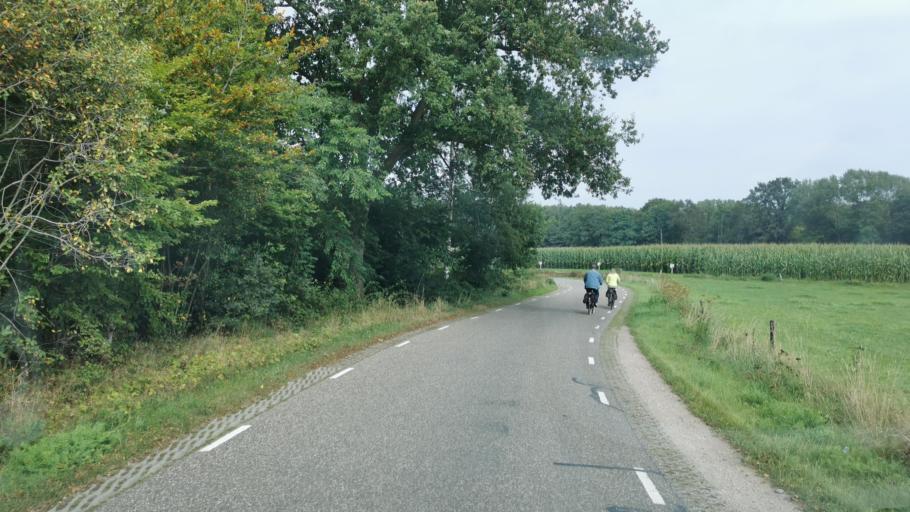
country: NL
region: Overijssel
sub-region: Gemeente Losser
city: Losser
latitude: 52.2823
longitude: 7.0209
